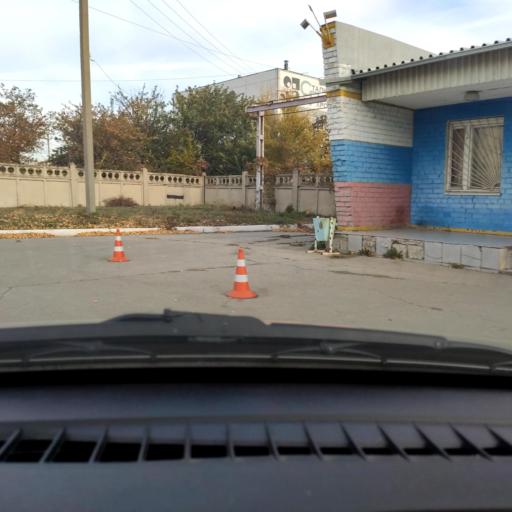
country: RU
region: Samara
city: Tol'yatti
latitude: 53.5585
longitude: 49.3310
